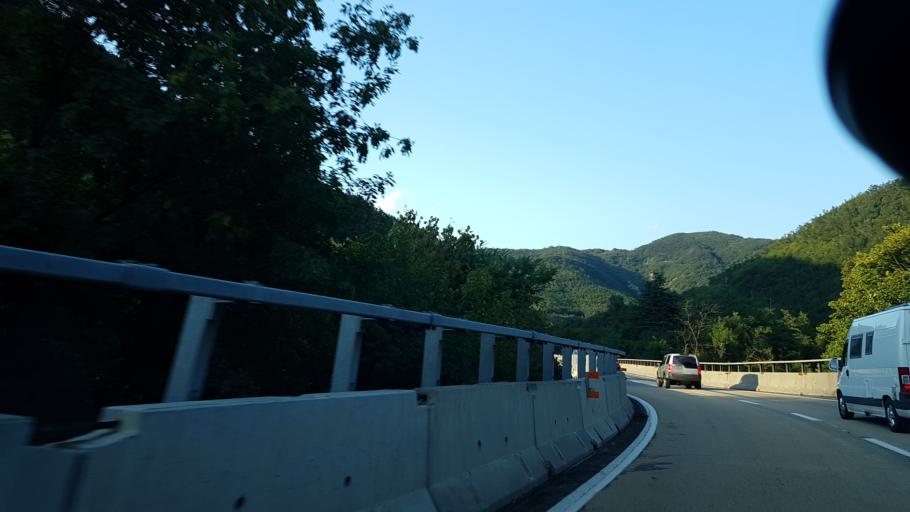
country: IT
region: Liguria
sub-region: Provincia di Genova
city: Isola del Cantone
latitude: 44.6585
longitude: 8.9256
